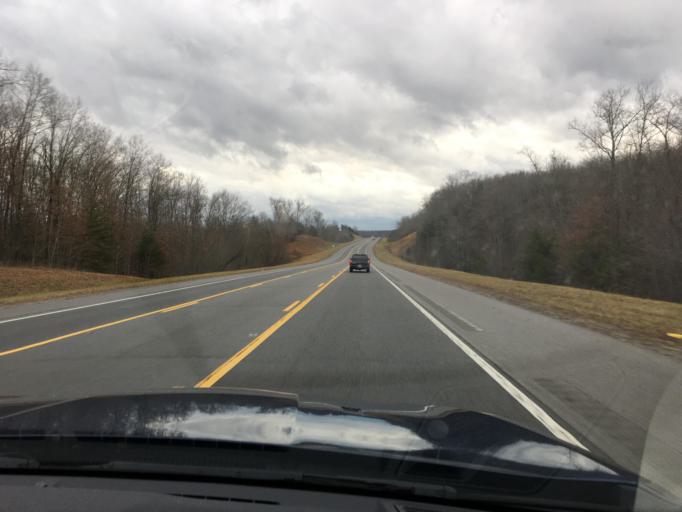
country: US
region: Tennessee
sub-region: Cumberland County
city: Crossville
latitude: 35.9455
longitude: -84.9926
